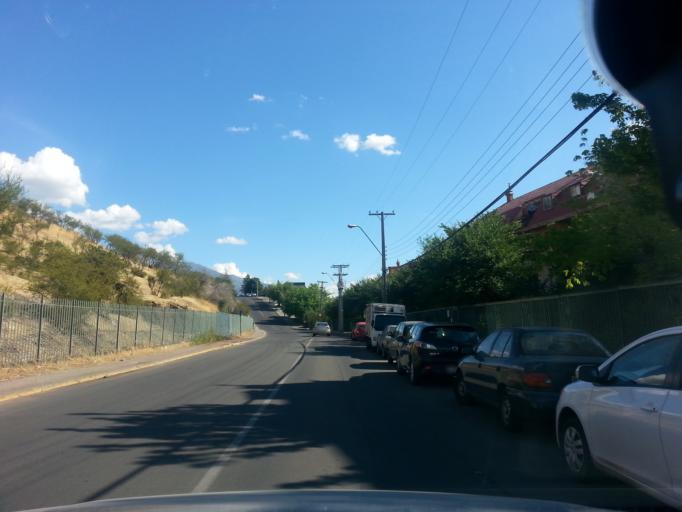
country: CL
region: Santiago Metropolitan
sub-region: Provincia de Santiago
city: Villa Presidente Frei, Nunoa, Santiago, Chile
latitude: -33.4078
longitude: -70.5332
